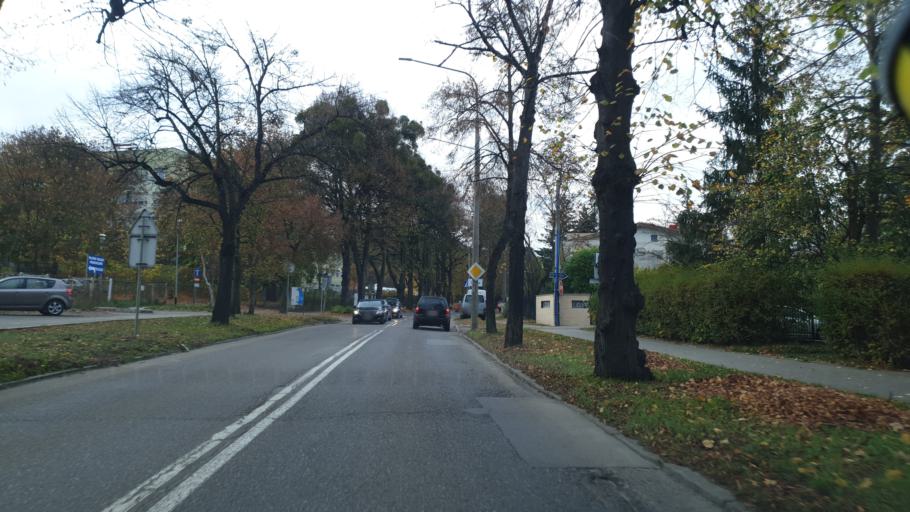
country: PL
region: Pomeranian Voivodeship
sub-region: Sopot
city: Sopot
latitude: 54.3945
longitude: 18.5668
